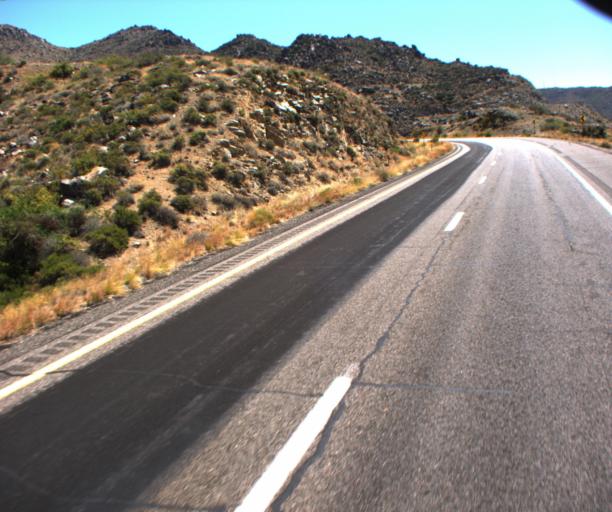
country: US
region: Arizona
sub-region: Yavapai County
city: Congress
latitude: 34.2037
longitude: -112.7894
